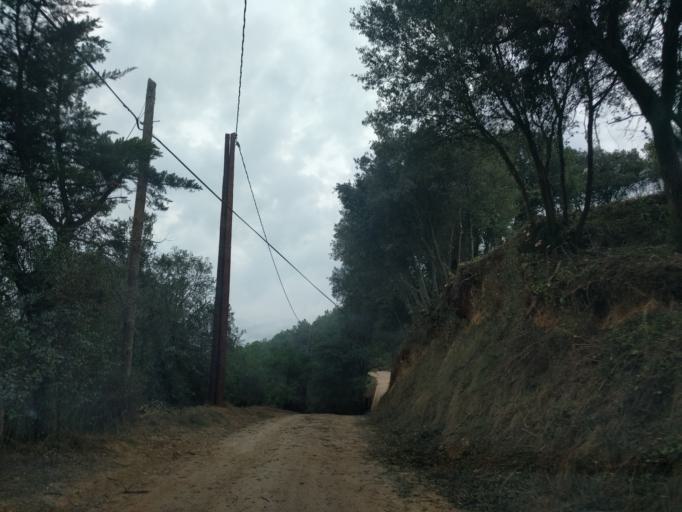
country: ES
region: Catalonia
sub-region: Provincia de Girona
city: la Cellera de Ter
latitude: 41.9705
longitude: 2.6300
